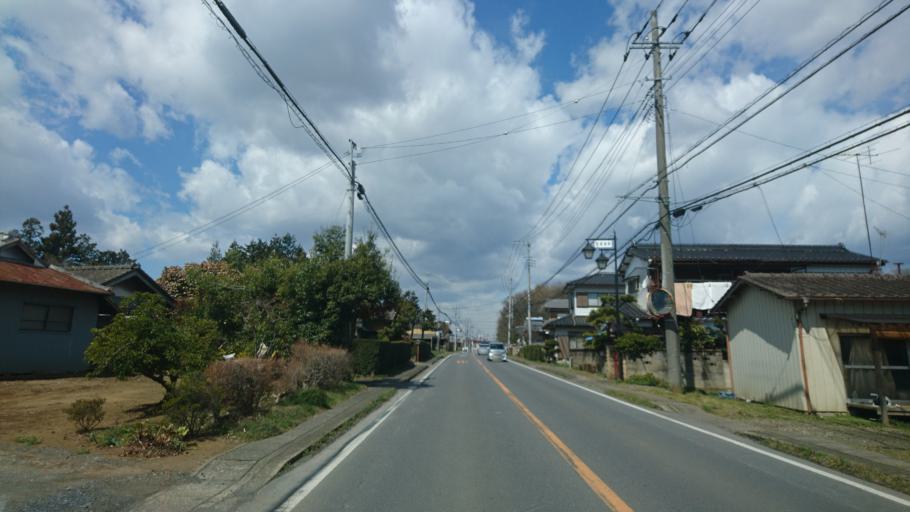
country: JP
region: Ibaraki
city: Ishige
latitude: 36.2034
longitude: 139.9450
